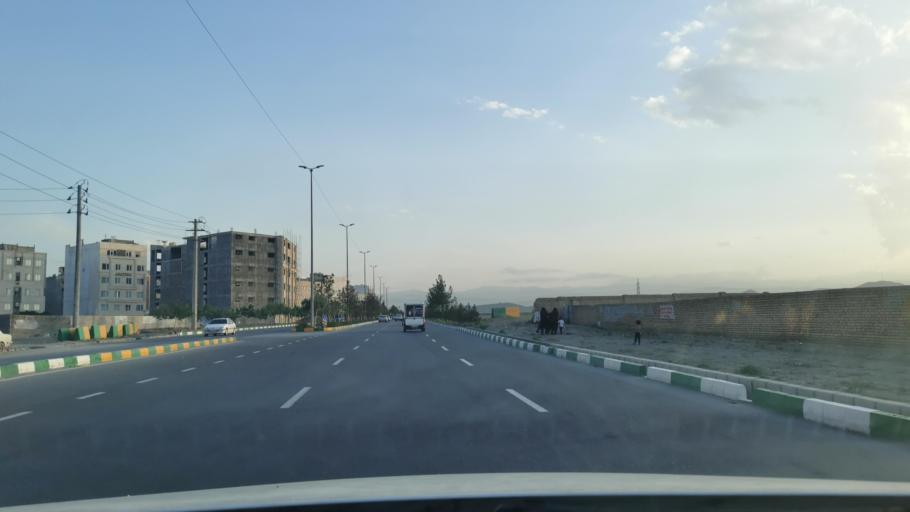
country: IR
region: Razavi Khorasan
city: Mashhad
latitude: 36.3936
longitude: 59.4724
